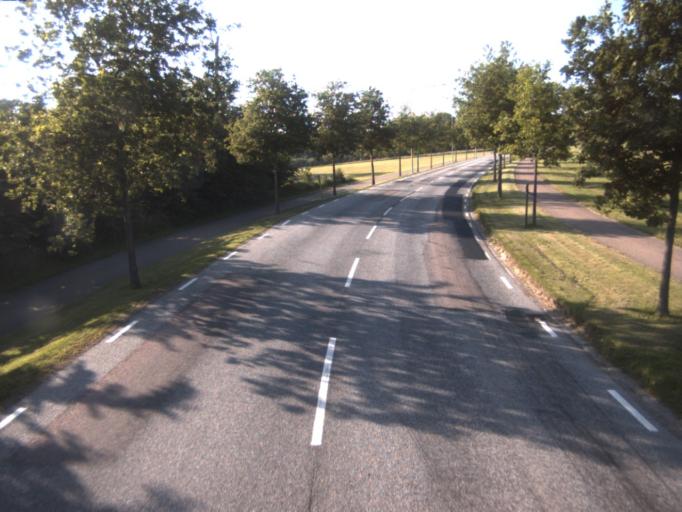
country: SE
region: Skane
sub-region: Helsingborg
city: Helsingborg
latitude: 56.0808
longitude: 12.6632
